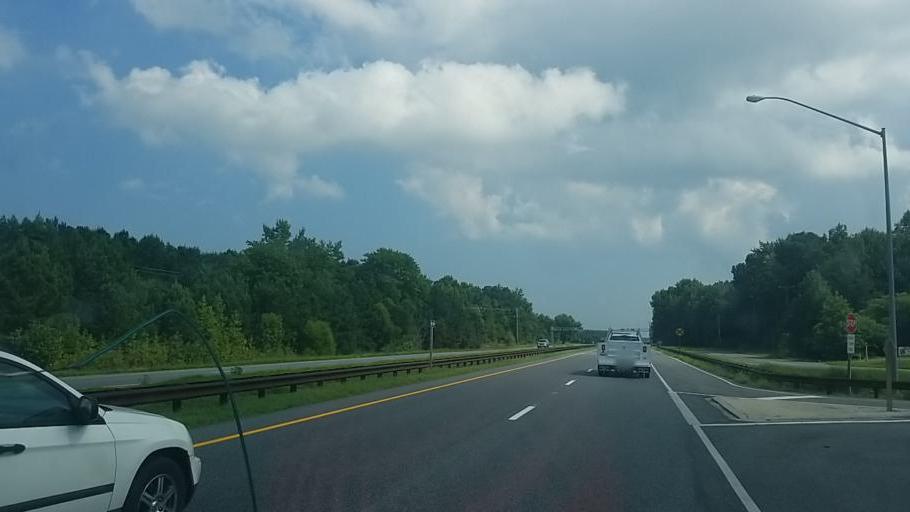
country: US
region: Delaware
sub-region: Sussex County
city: Selbyville
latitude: 38.4376
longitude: -75.2247
